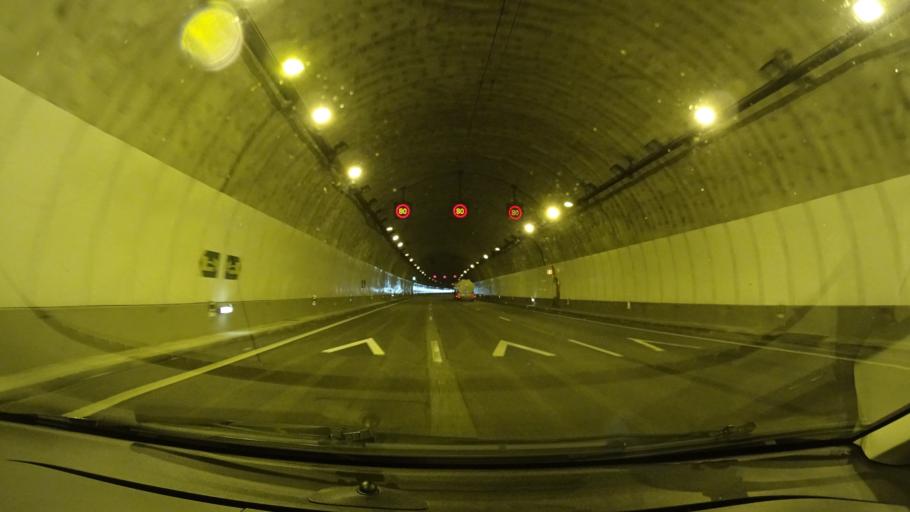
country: ES
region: Andalusia
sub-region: Provincia de Sevilla
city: El Ronquillo
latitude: 37.6491
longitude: -6.1592
